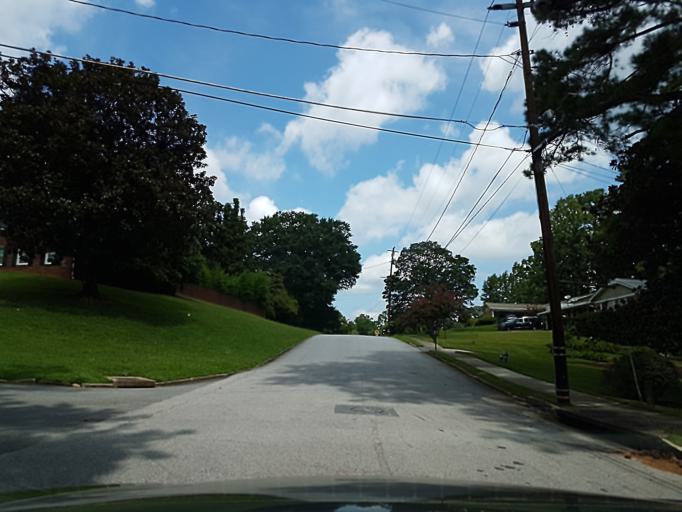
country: US
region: Georgia
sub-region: DeKalb County
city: North Druid Hills
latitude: 33.8263
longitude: -84.3201
